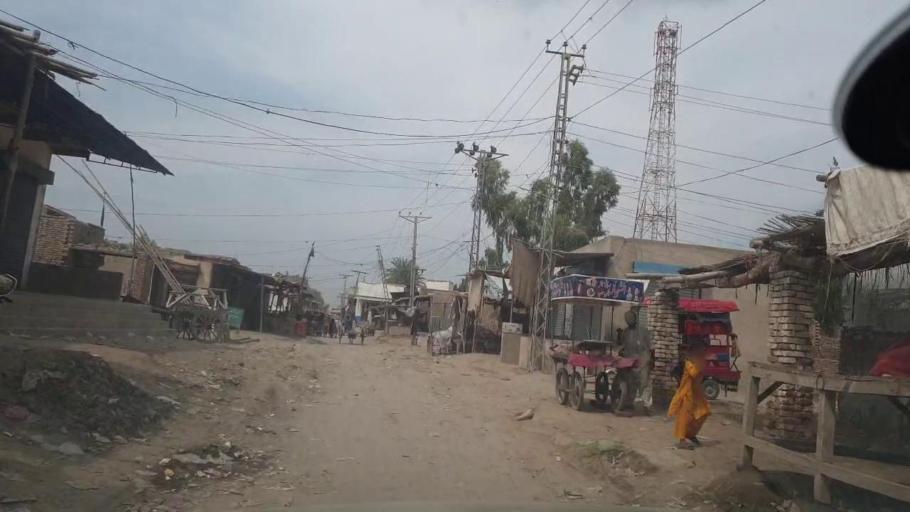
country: PK
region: Sindh
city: Jacobabad
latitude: 28.2689
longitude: 68.4379
